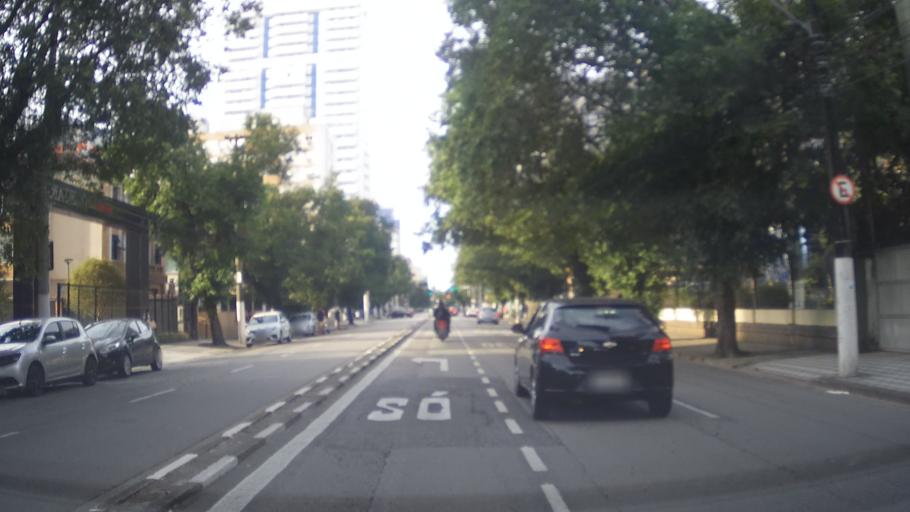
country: BR
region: Sao Paulo
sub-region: Santos
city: Santos
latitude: -23.9634
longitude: -46.3234
